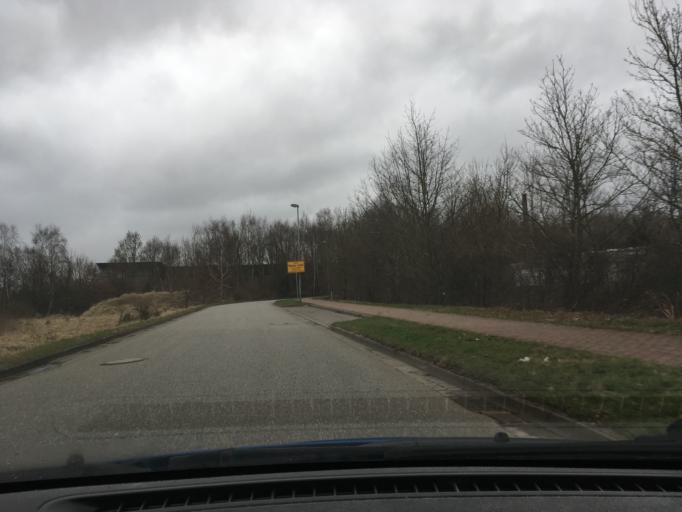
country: DE
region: Lower Saxony
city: Winsen
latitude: 53.3701
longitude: 10.2295
